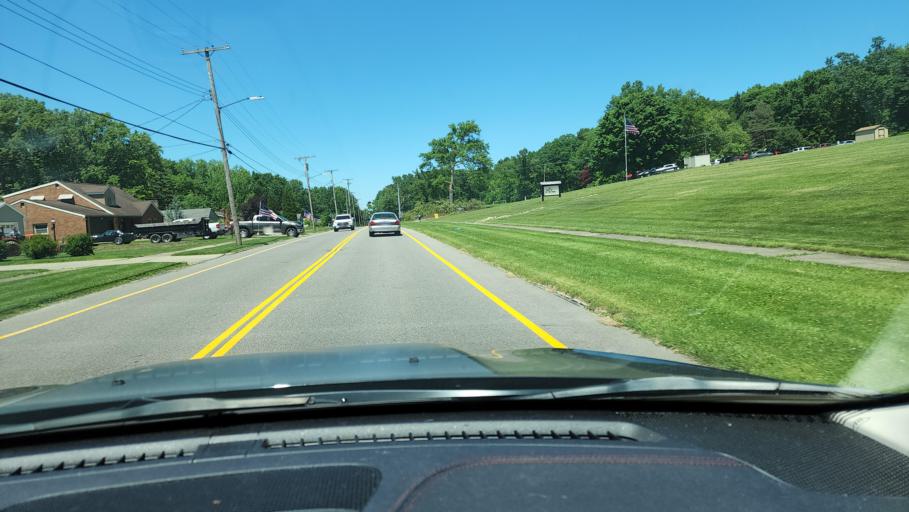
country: US
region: Ohio
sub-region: Trumbull County
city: Niles
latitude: 41.1876
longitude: -80.7448
